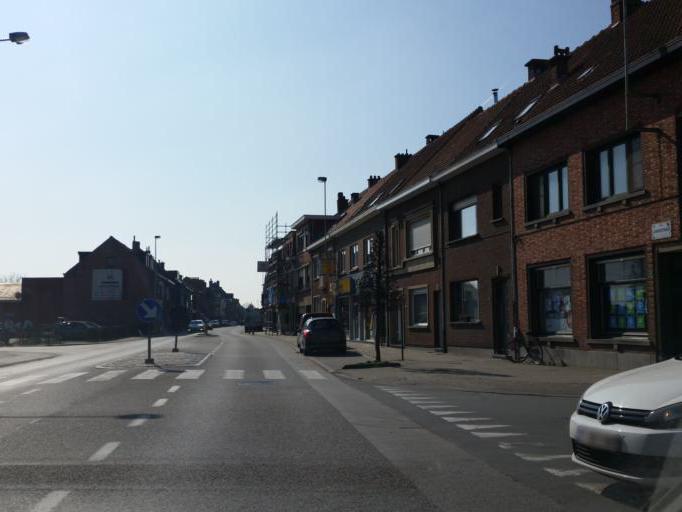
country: BE
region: Flanders
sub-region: Provincie Oost-Vlaanderen
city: Kruibeke
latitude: 51.1762
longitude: 4.3158
